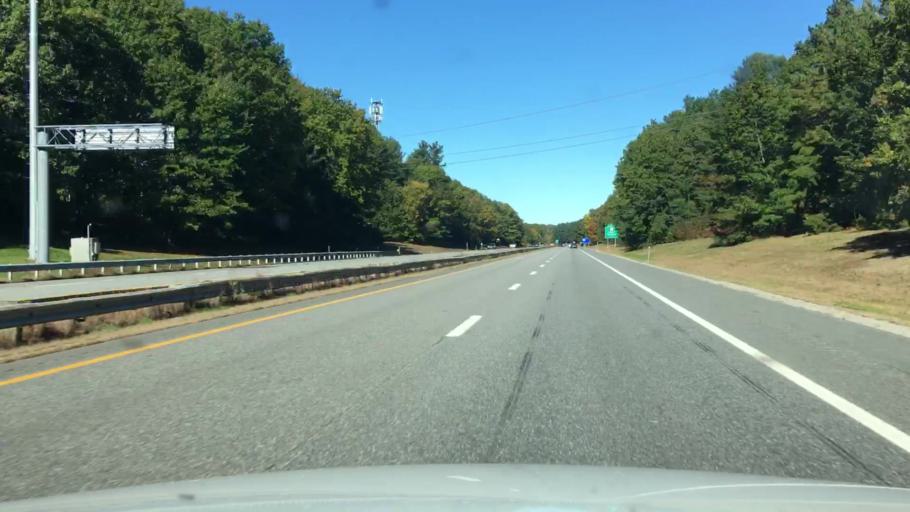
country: US
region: New Hampshire
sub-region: Strafford County
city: Dover
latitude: 43.1651
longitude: -70.8558
